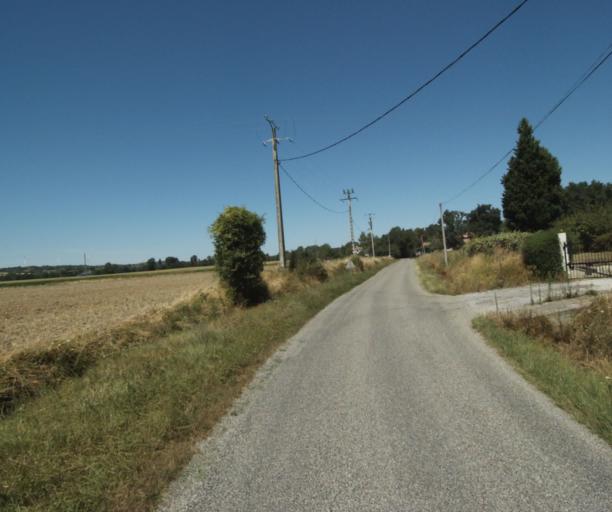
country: FR
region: Midi-Pyrenees
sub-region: Departement de la Haute-Garonne
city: Revel
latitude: 43.4537
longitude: 1.9464
